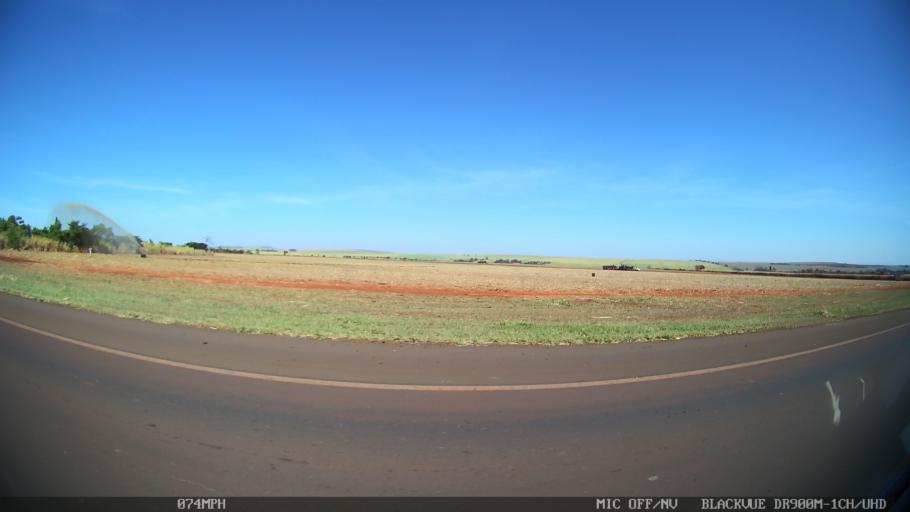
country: BR
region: Sao Paulo
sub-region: Ipua
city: Ipua
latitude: -20.4625
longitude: -48.1375
